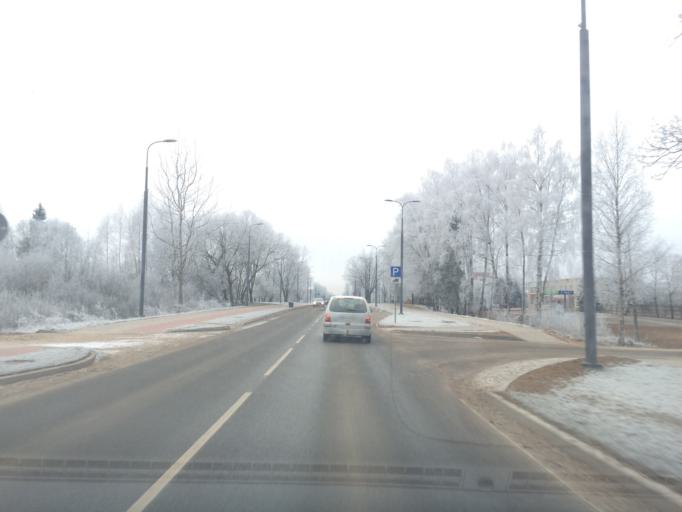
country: LV
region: Rezekne
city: Rezekne
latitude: 56.5358
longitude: 27.3486
